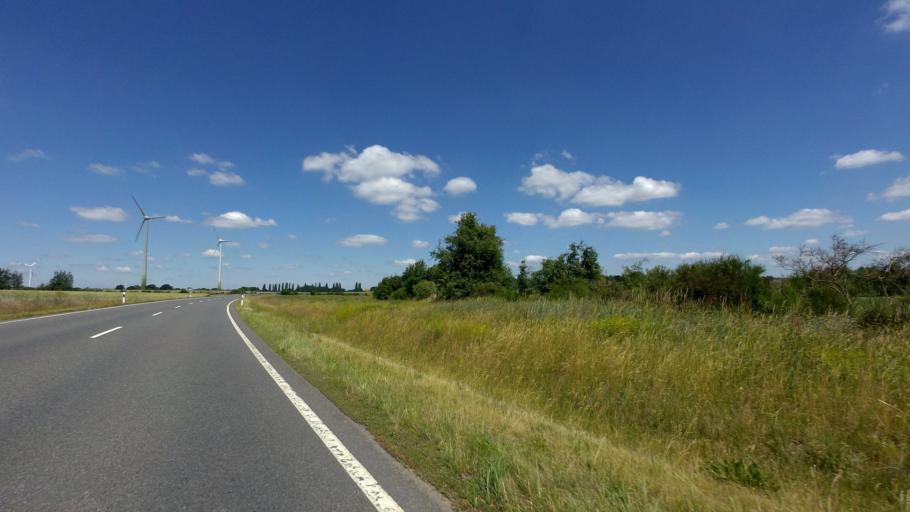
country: DE
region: Brandenburg
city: Luckau
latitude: 51.8355
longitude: 13.6791
